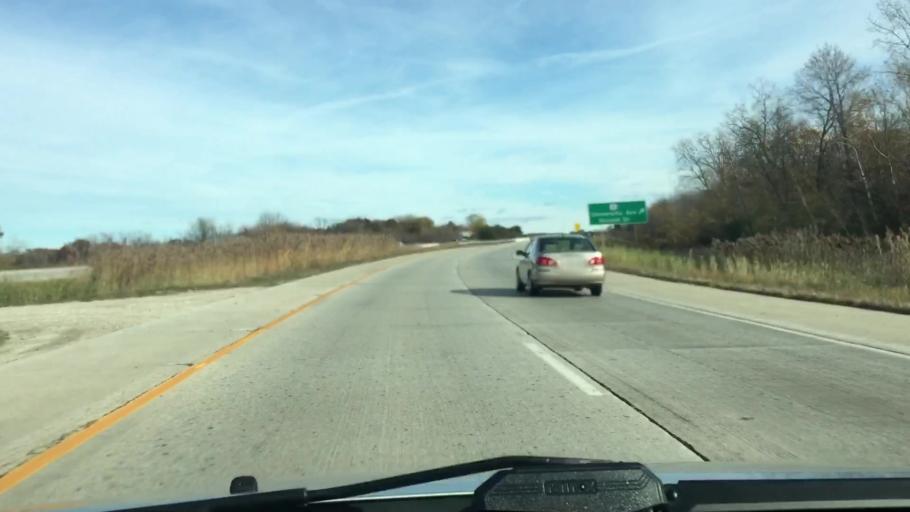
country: US
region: Wisconsin
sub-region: Brown County
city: Green Bay
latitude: 44.5251
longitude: -87.9438
